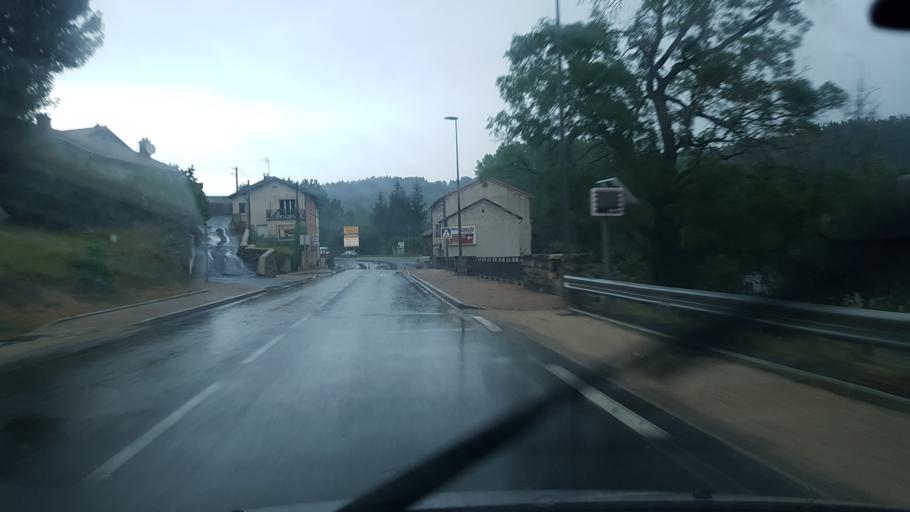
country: FR
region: Auvergne
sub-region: Departement de la Haute-Loire
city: Saint-Paulien
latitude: 45.0989
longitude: 3.7976
